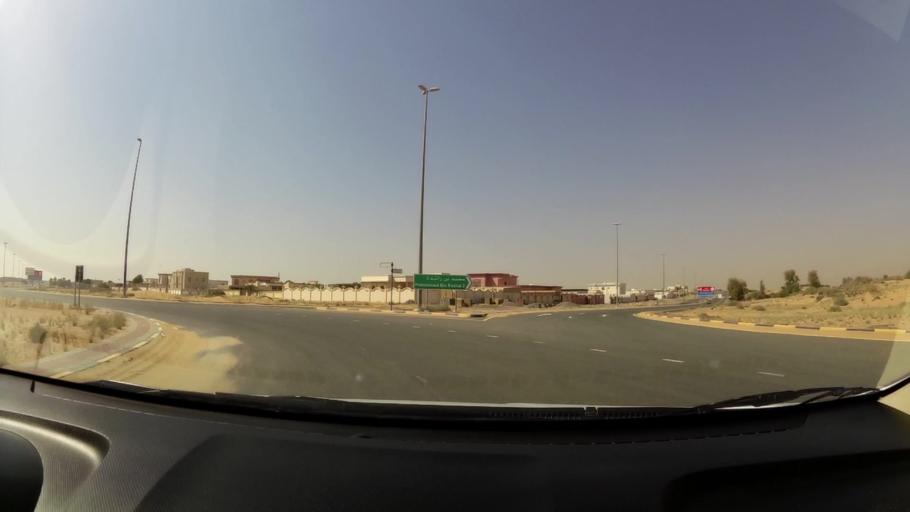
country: AE
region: Umm al Qaywayn
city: Umm al Qaywayn
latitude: 25.4692
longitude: 55.6145
